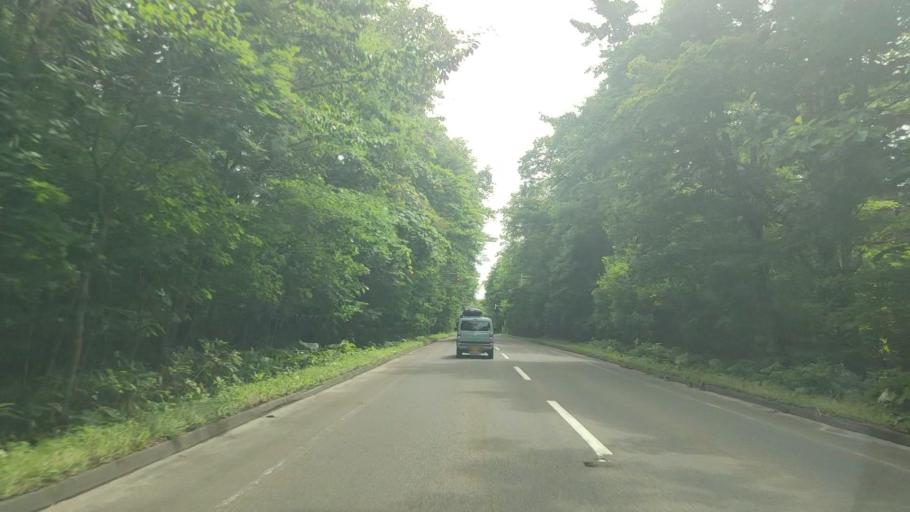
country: JP
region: Hokkaido
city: Tomakomai
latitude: 42.7690
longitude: 141.4393
